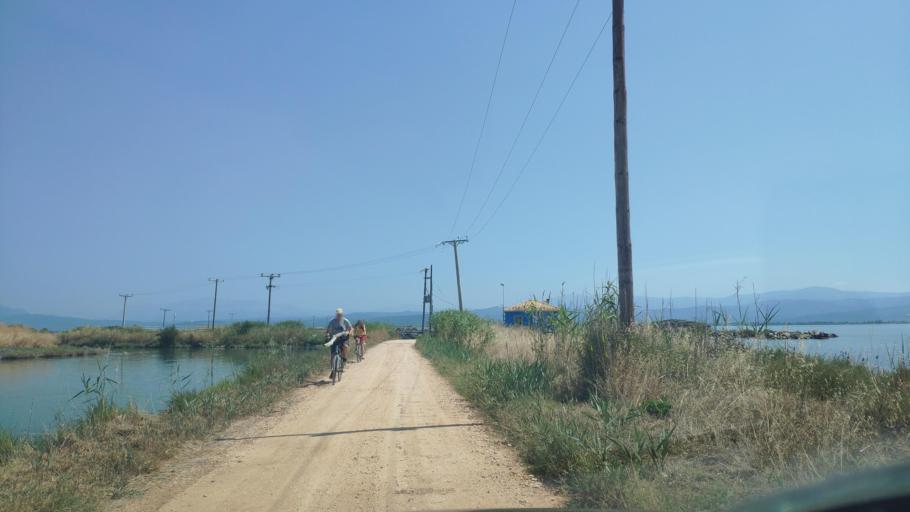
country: GR
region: Epirus
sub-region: Nomos Artas
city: Aneza
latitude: 39.0152
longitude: 20.9288
